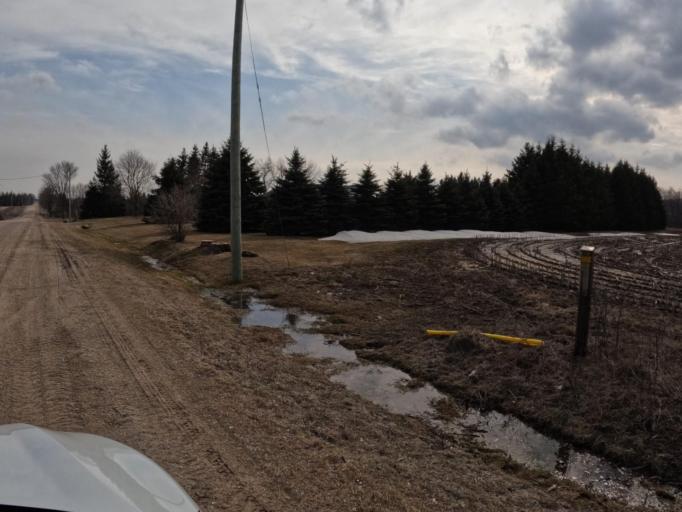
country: CA
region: Ontario
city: Shelburne
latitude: 43.9148
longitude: -80.3047
